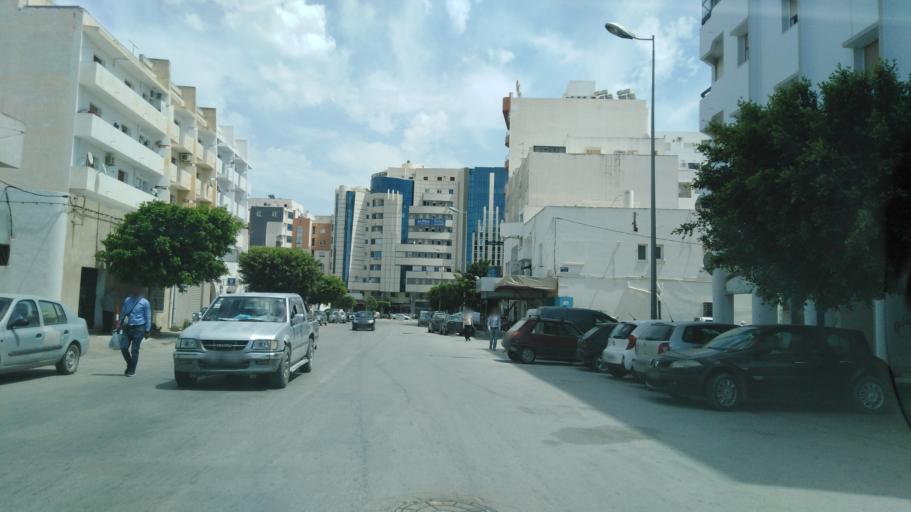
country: TN
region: Safaqis
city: Sfax
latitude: 34.7436
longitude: 10.7532
